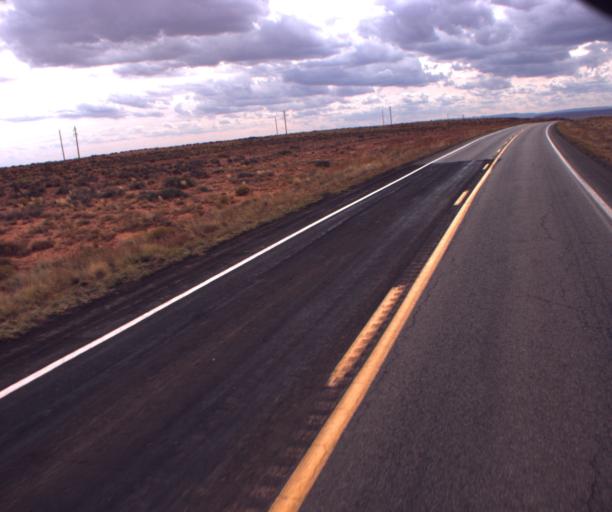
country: US
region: Arizona
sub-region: Navajo County
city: Kayenta
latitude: 36.9002
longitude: -109.7912
